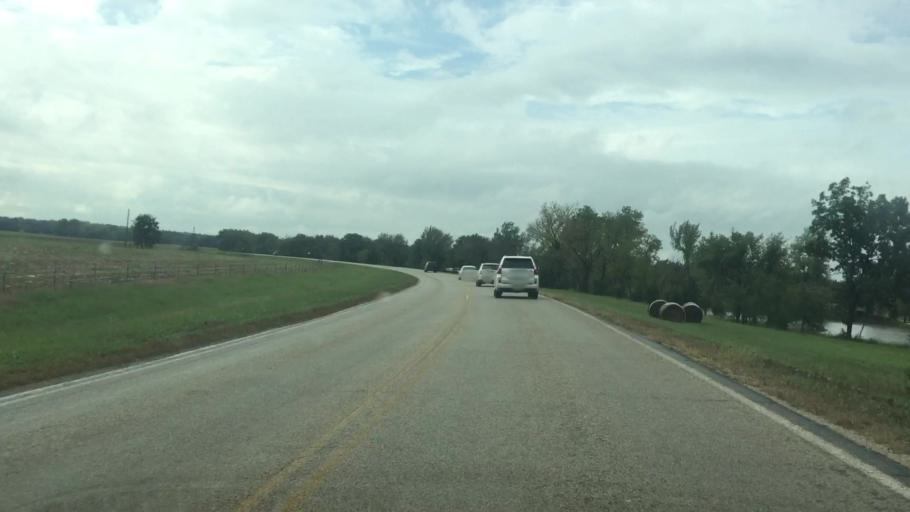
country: US
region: Kansas
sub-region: Allen County
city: Iola
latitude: 37.8820
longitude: -95.4353
